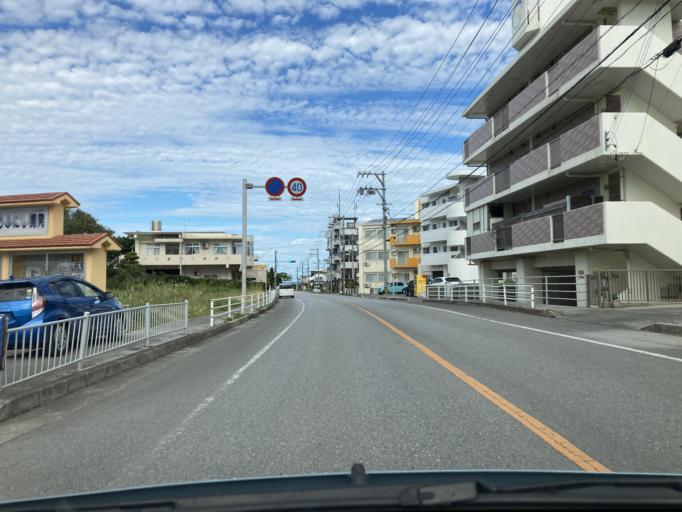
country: JP
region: Okinawa
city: Ishikawa
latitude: 26.4202
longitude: 127.7322
